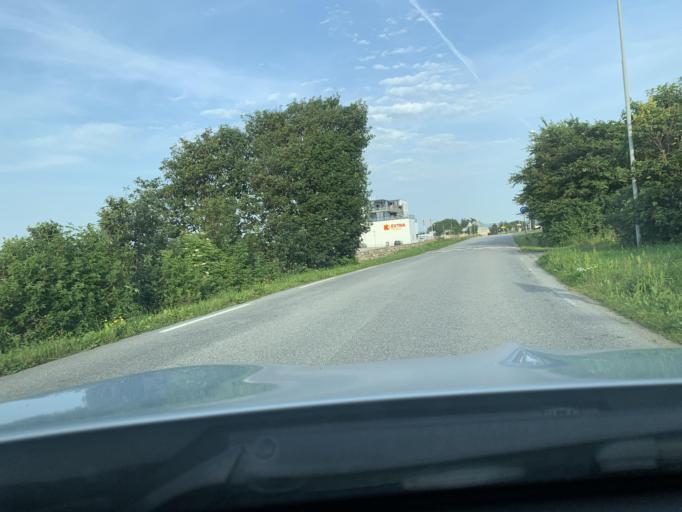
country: NO
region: Rogaland
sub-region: Time
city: Bryne
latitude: 58.7189
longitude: 5.5651
